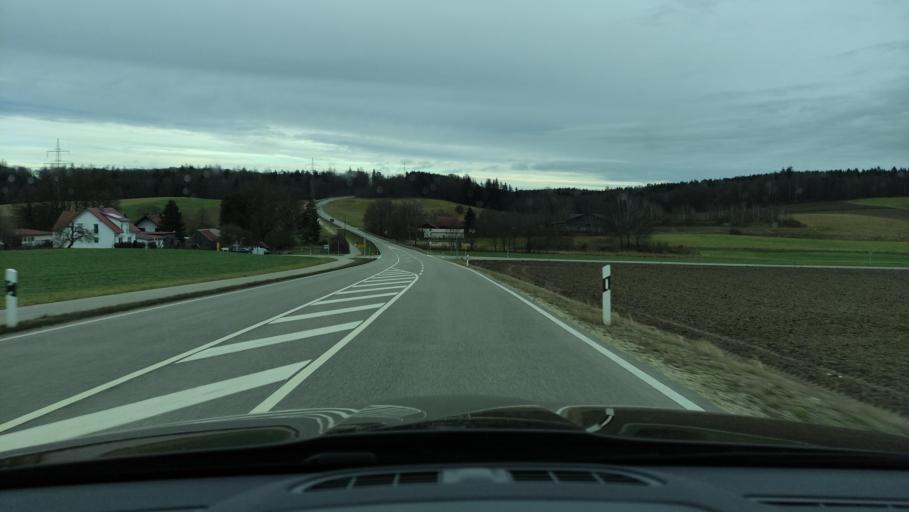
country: DE
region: Bavaria
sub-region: Swabia
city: Roggenburg
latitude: 48.2425
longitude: 10.2278
